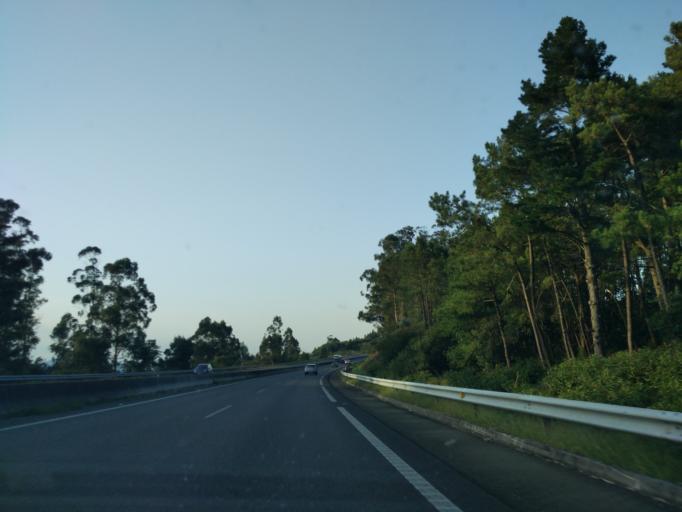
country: ES
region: Galicia
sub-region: Provincia de Pontevedra
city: Valga
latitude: 42.6500
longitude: -8.6516
